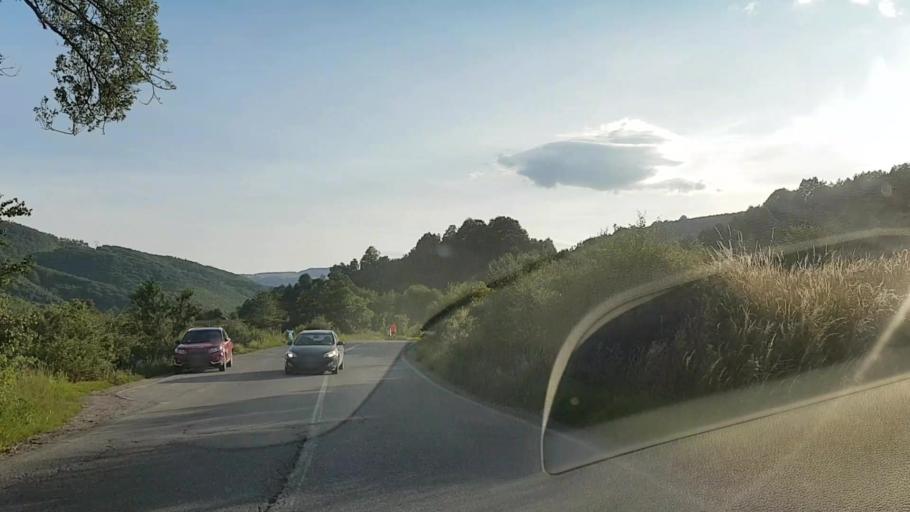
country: RO
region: Harghita
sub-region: Comuna Praid
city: Praid
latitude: 46.5685
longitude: 25.1661
